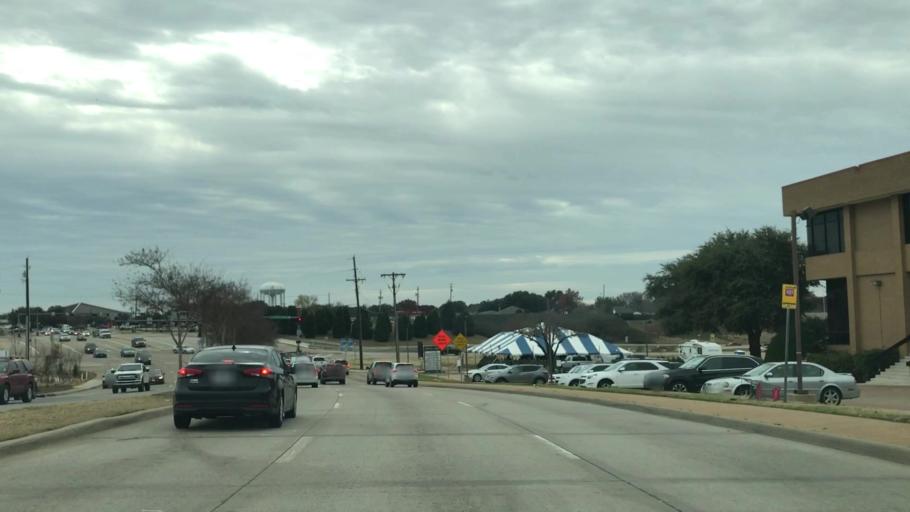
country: US
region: Texas
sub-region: Dallas County
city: Carrollton
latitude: 32.9874
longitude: -96.8909
